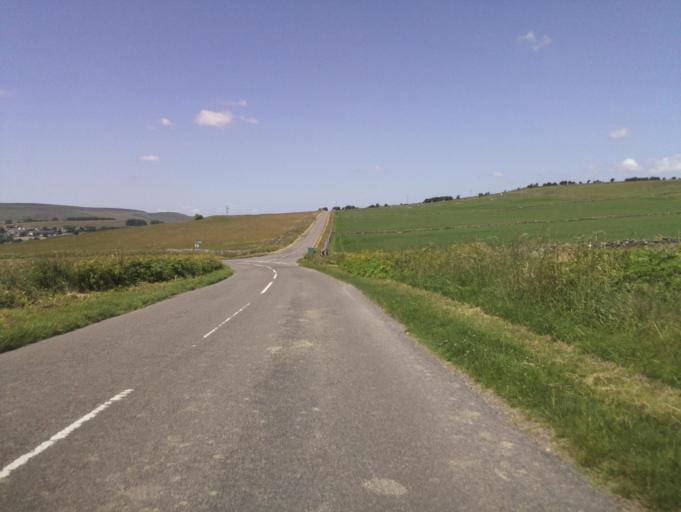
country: GB
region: England
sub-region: Derbyshire
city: Buxton
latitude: 53.2791
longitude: -1.8464
